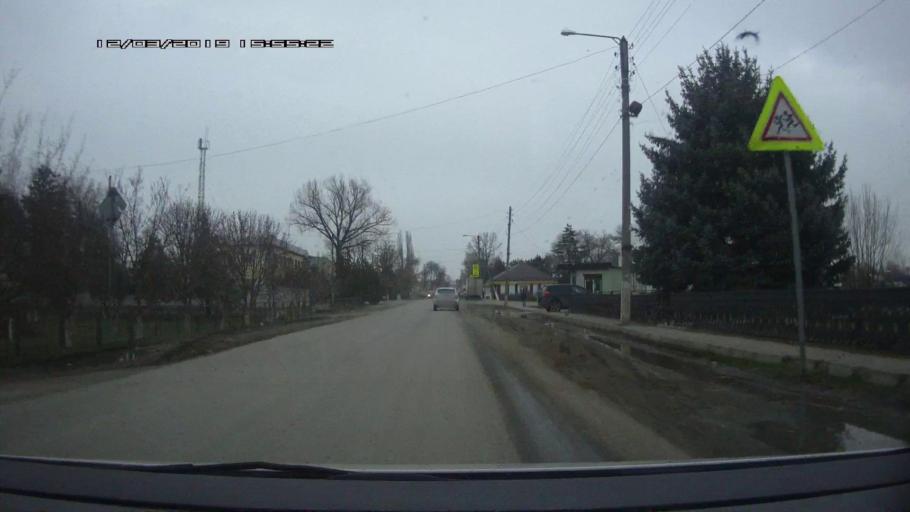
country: RU
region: Rostov
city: Novobataysk
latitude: 46.8962
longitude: 39.7796
